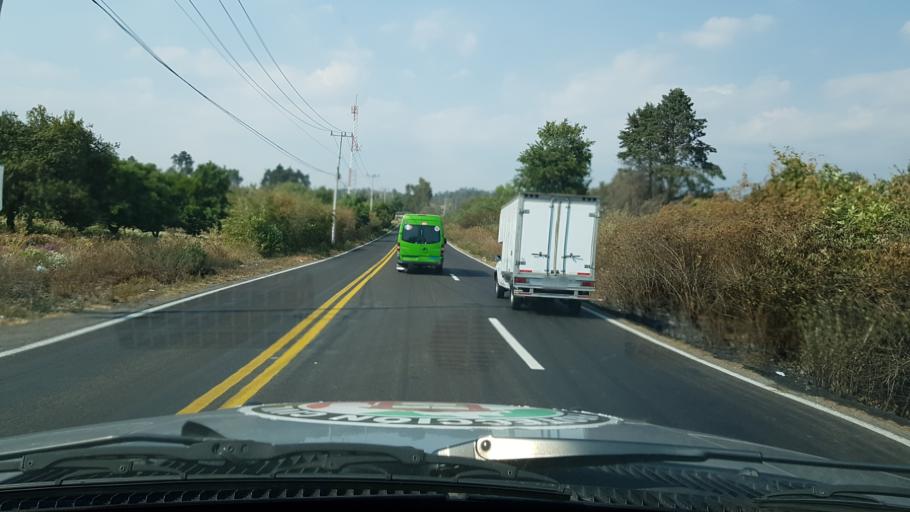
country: MX
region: Mexico
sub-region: Ozumba
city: San Jose Tlacotitlan
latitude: 19.0015
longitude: -98.8221
